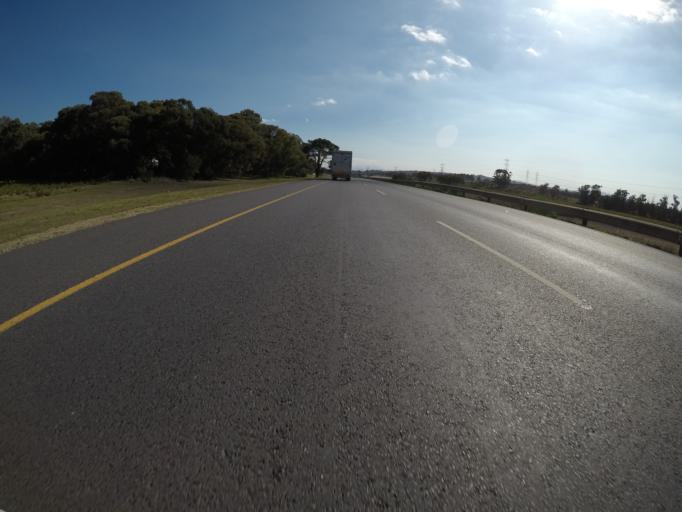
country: ZA
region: Western Cape
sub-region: City of Cape Town
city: Kraaifontein
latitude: -33.8828
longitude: 18.7555
